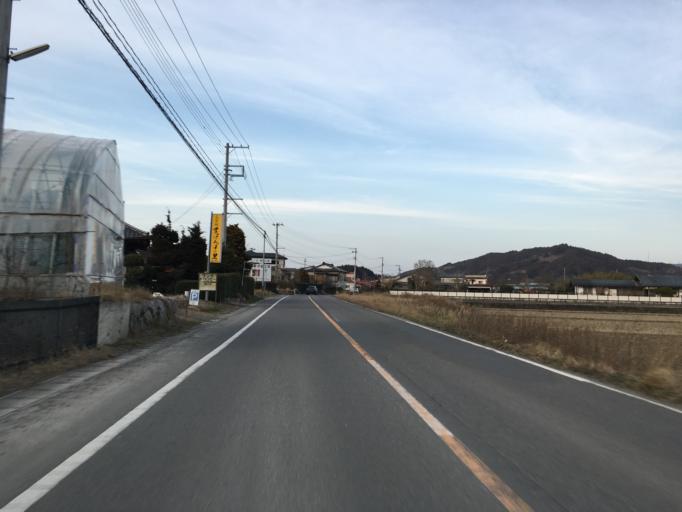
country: JP
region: Ibaraki
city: Daigo
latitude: 36.9393
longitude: 140.4053
